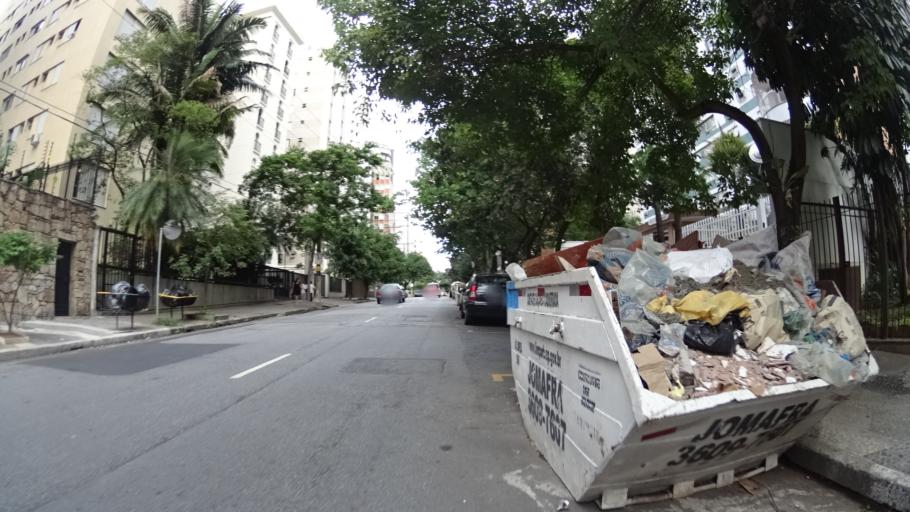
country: BR
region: Sao Paulo
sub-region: Sao Paulo
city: Sao Paulo
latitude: -23.5805
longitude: -46.6735
